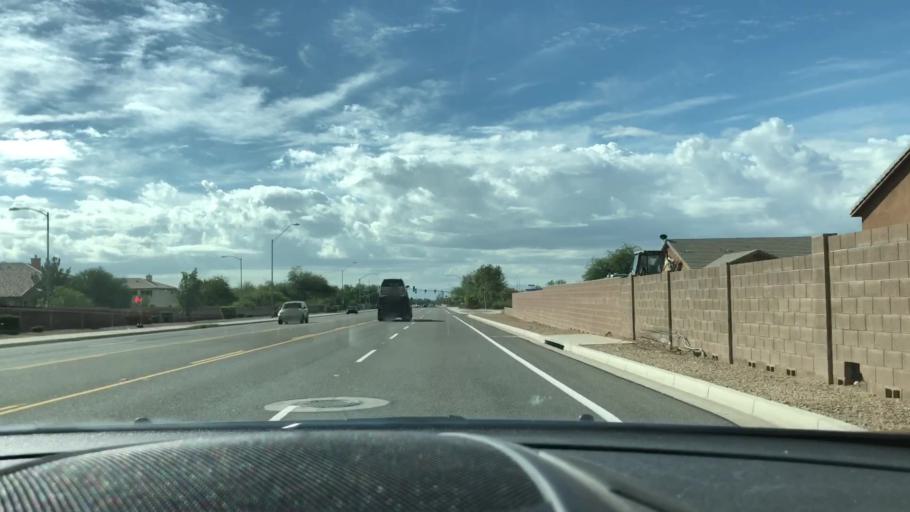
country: US
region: Arizona
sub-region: Maricopa County
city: Sun City
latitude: 33.6989
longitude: -112.2377
